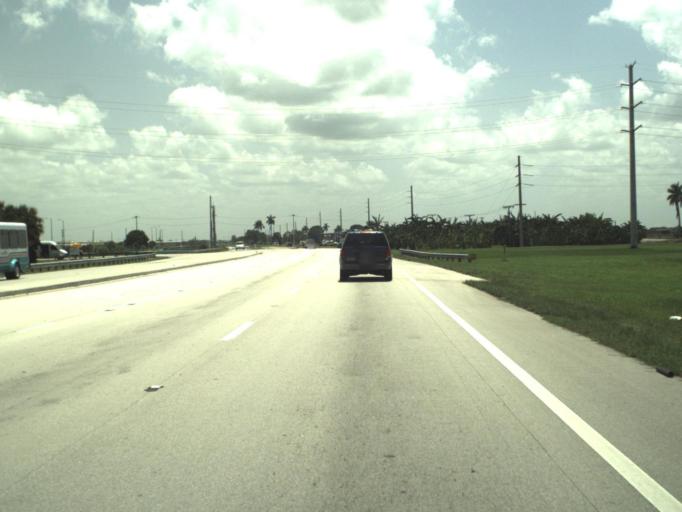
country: US
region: Florida
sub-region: Palm Beach County
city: Belle Glade
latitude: 26.7226
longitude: -80.6679
